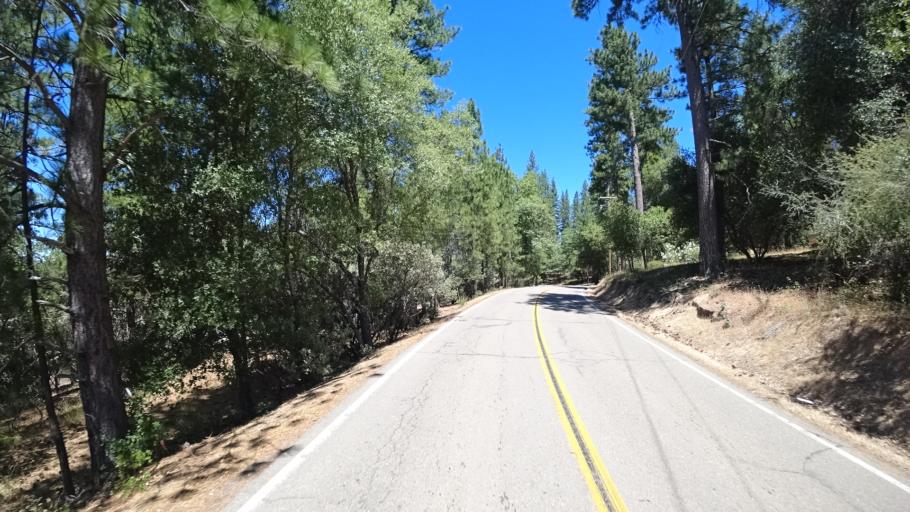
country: US
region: California
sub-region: Amador County
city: Pioneer
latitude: 38.3748
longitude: -120.5097
